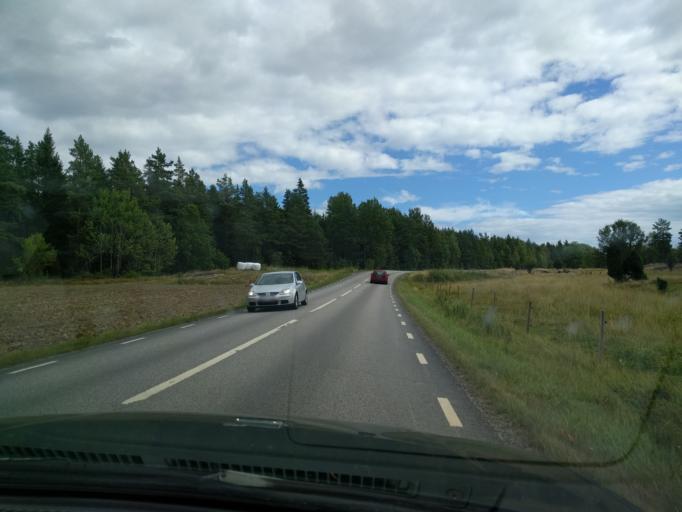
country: SE
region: Soedermanland
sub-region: Nykopings Kommun
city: Svalsta
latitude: 58.5206
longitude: 16.8099
